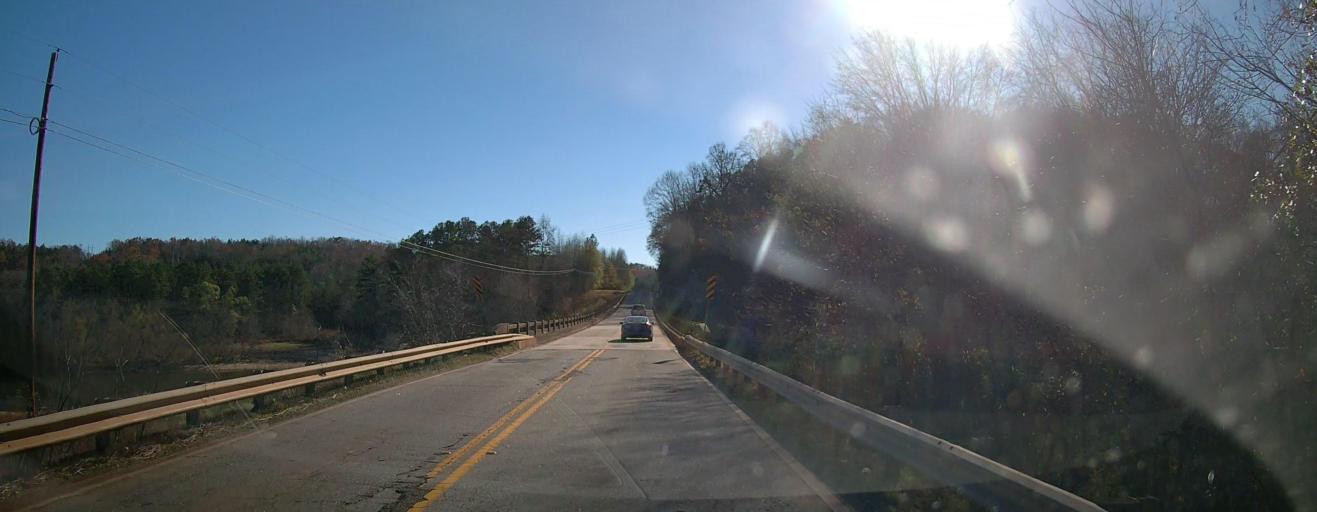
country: US
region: Georgia
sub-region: Hall County
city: Lula
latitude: 34.4146
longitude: -83.7085
